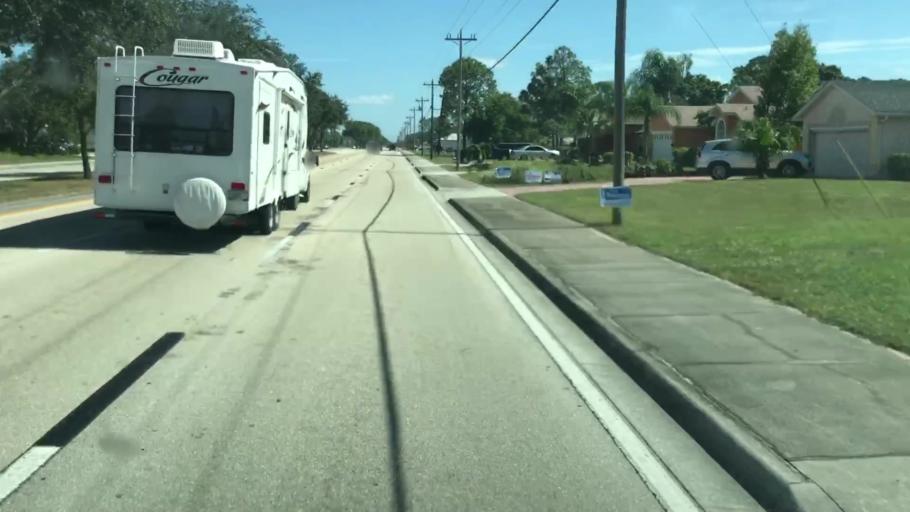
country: US
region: Florida
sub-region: Lee County
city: Gateway
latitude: 26.6169
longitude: -81.7038
